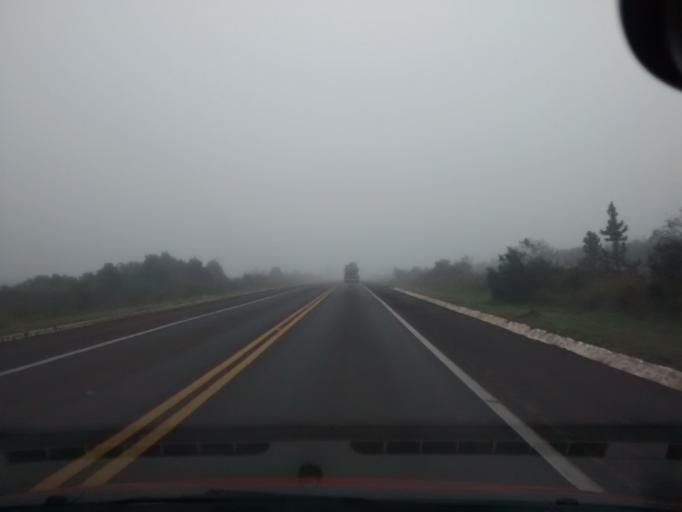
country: BR
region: Rio Grande do Sul
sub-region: Vacaria
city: Vacaria
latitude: -28.3803
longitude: -50.8413
